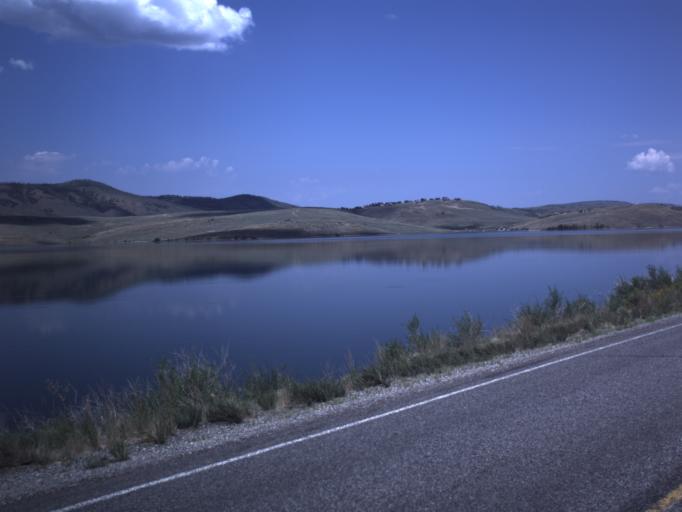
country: US
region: Utah
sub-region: Carbon County
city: Helper
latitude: 39.7712
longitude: -111.1397
